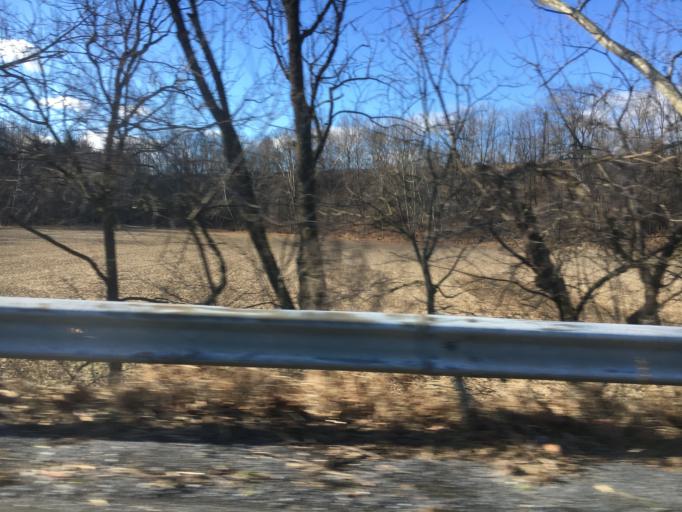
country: US
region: Pennsylvania
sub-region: Lehigh County
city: Stiles
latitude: 40.6322
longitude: -75.5407
